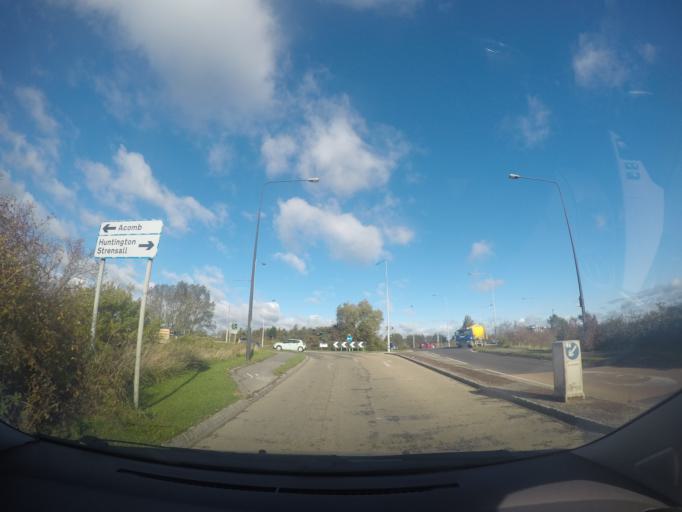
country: GB
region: England
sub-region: City of York
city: Haxby
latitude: 54.0006
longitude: -1.0728
